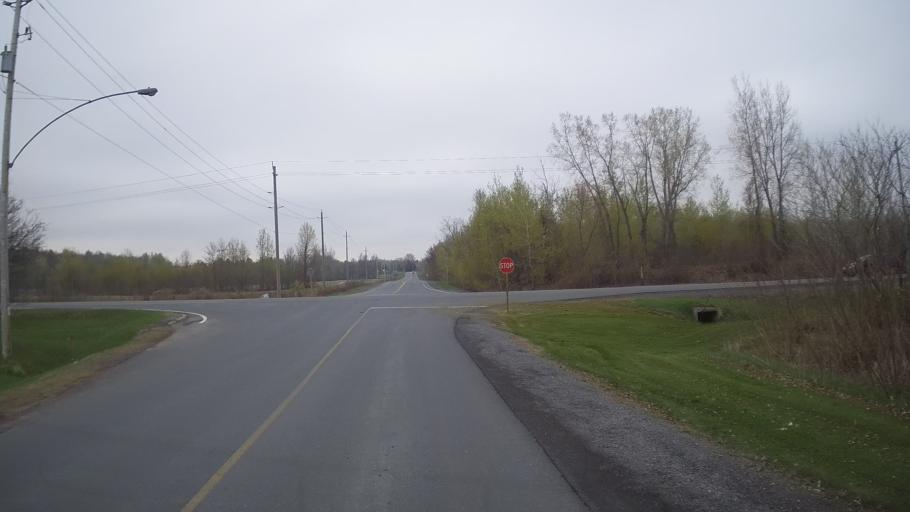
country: CA
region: Ontario
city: Hawkesbury
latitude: 45.5720
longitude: -74.5237
